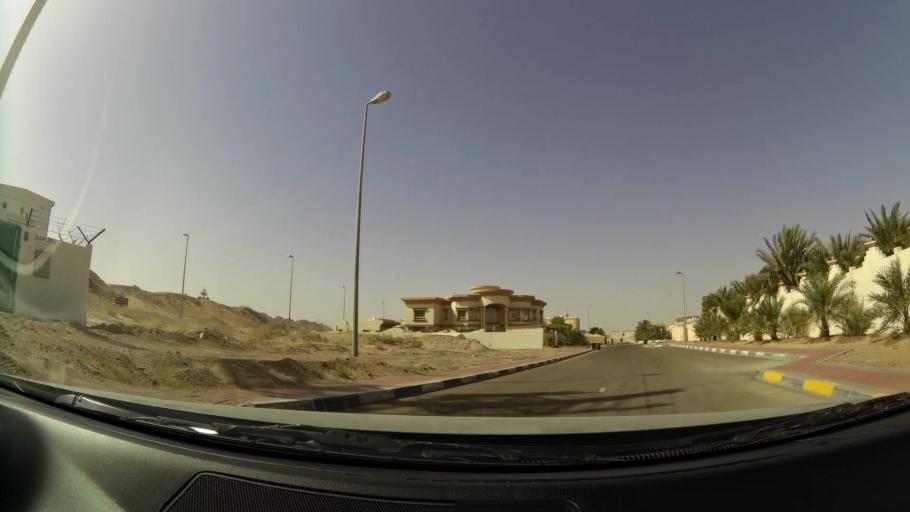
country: OM
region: Al Buraimi
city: Al Buraymi
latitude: 24.3206
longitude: 55.8133
